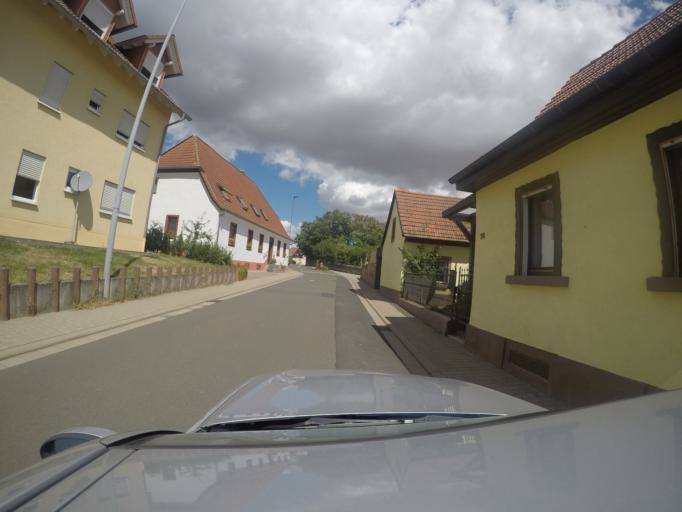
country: DE
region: Rheinland-Pfalz
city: Orbis
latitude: 49.6749
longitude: 7.9872
